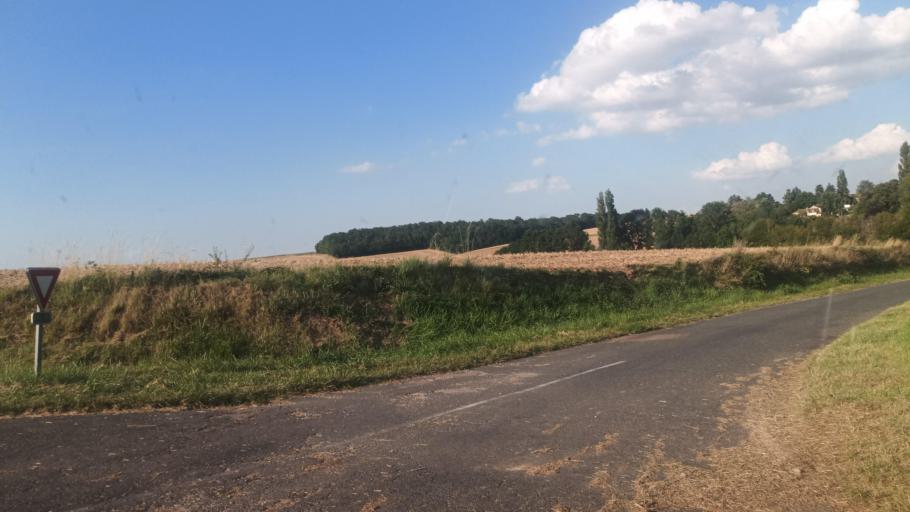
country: FR
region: Bourgogne
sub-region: Departement de l'Yonne
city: Saint-Valerien
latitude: 48.2251
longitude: 3.0647
